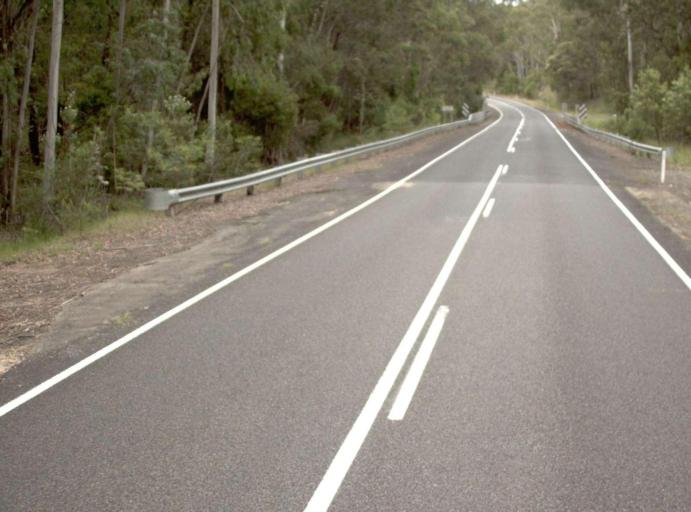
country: AU
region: New South Wales
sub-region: Bombala
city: Bombala
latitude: -37.2824
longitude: 149.2226
